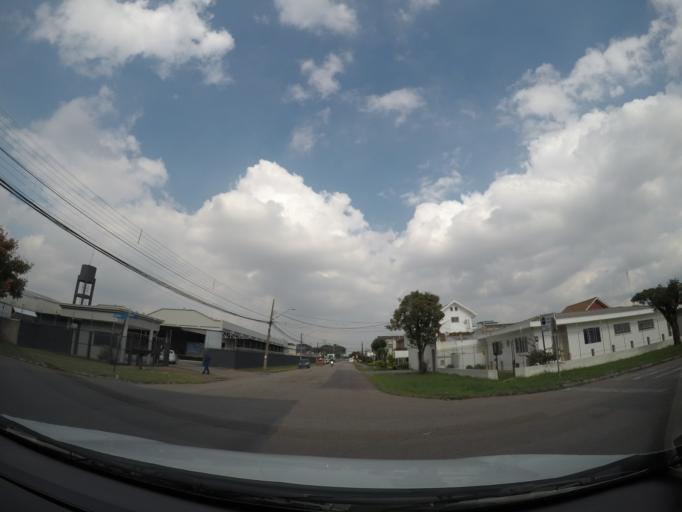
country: BR
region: Parana
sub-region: Curitiba
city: Curitiba
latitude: -25.4748
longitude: -49.2560
